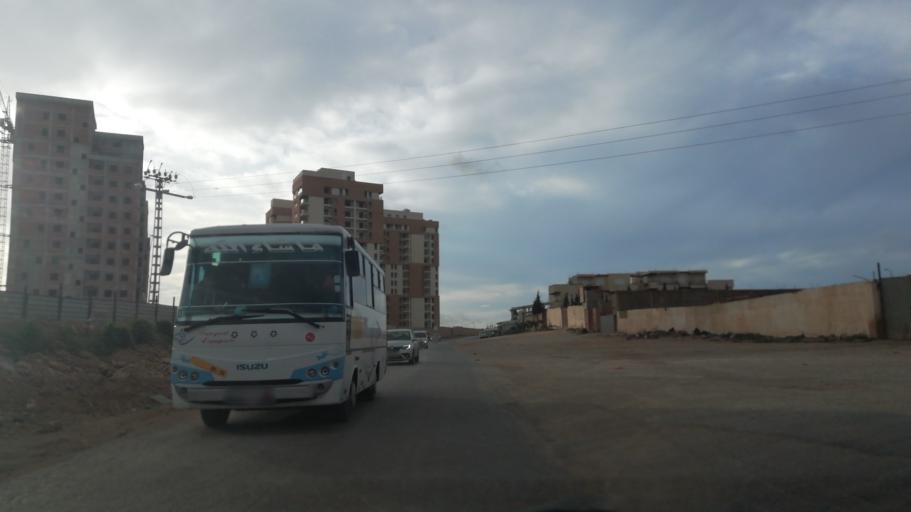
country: DZ
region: Oran
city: Bir el Djir
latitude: 35.7146
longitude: -0.5545
